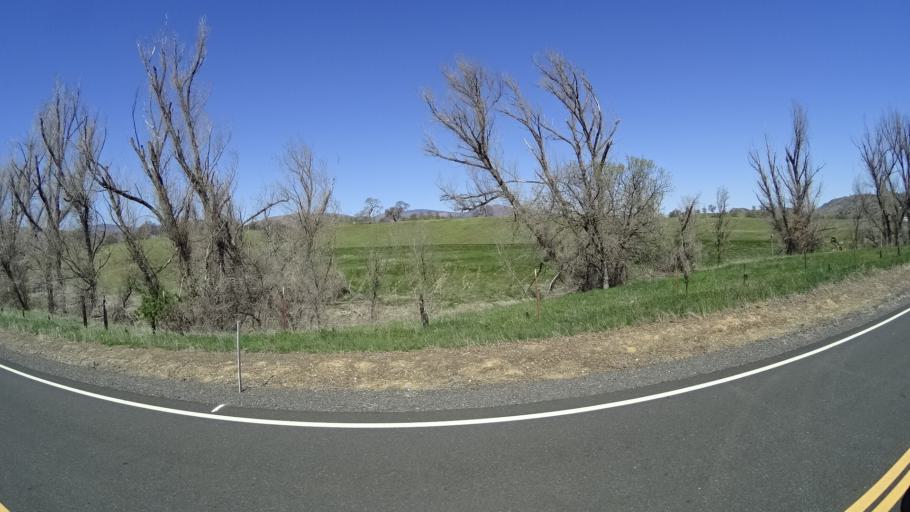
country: US
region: California
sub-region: Glenn County
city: Orland
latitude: 39.6621
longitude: -122.5289
